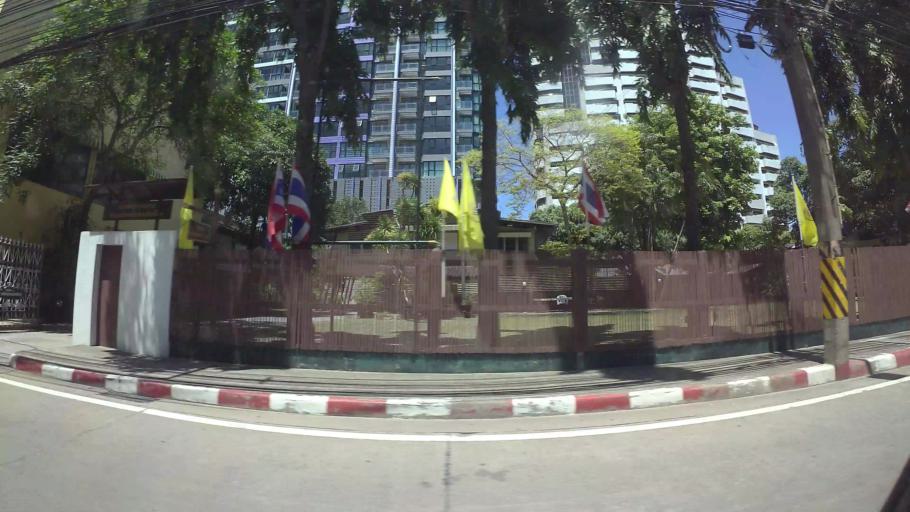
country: TH
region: Chon Buri
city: Si Racha
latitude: 13.1702
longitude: 100.9261
